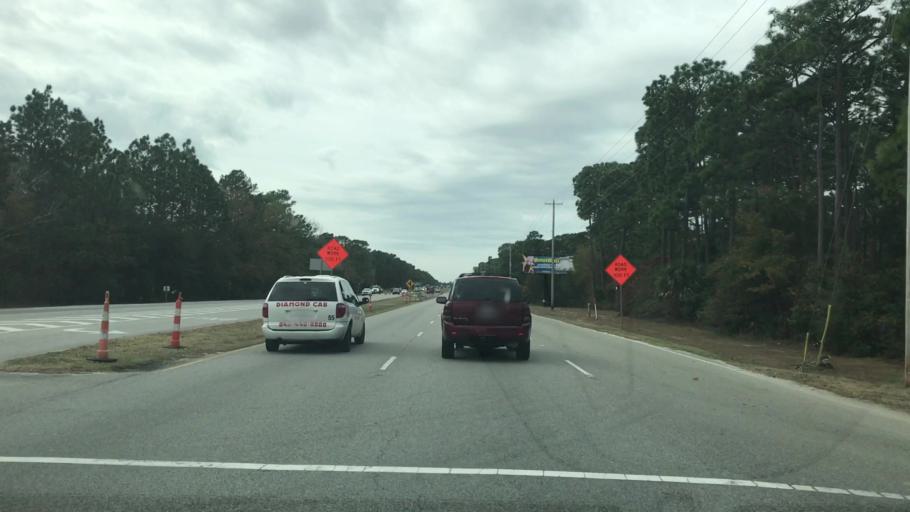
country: US
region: South Carolina
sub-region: Horry County
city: Myrtle Beach
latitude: 33.7564
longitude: -78.8252
